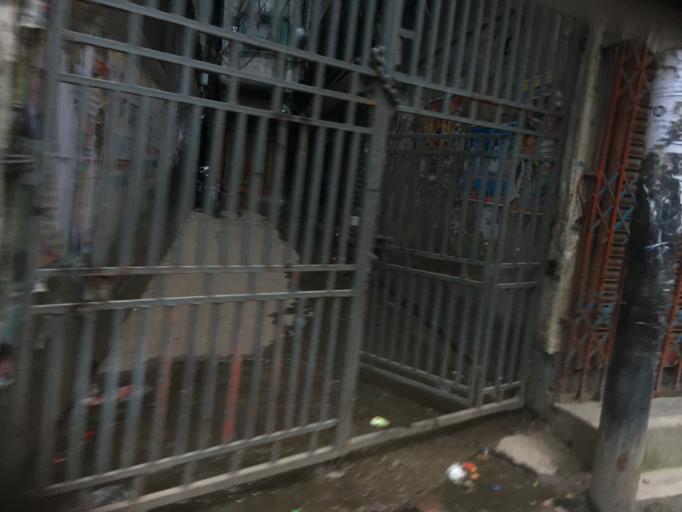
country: BD
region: Dhaka
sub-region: Dhaka
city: Dhaka
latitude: 23.7188
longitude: 90.4070
